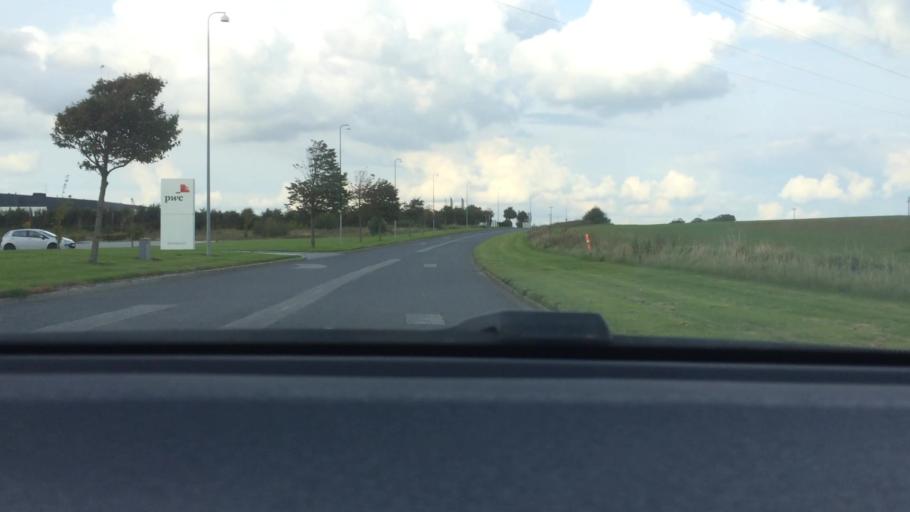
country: DK
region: South Denmark
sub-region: Vejle Kommune
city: Vejle
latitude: 55.7420
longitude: 9.5839
